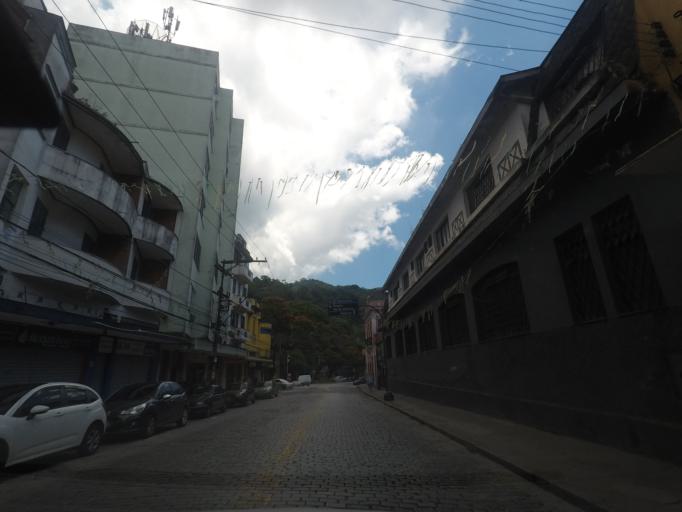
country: BR
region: Rio de Janeiro
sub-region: Petropolis
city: Petropolis
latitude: -22.5043
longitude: -43.1817
